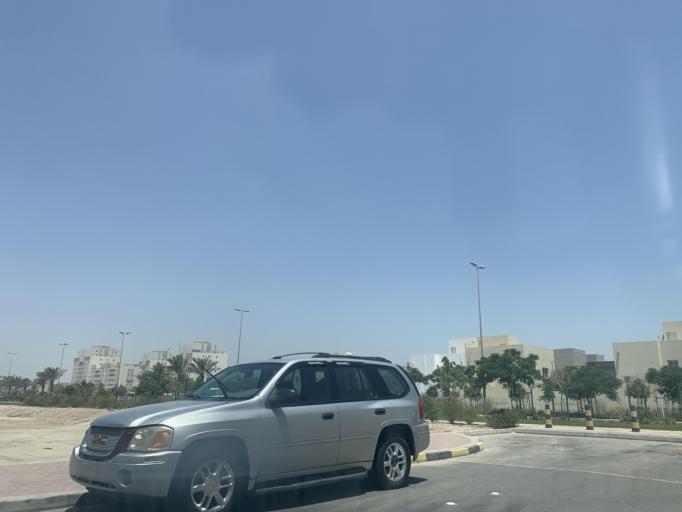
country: BH
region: Manama
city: Jidd Hafs
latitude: 26.2375
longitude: 50.4684
